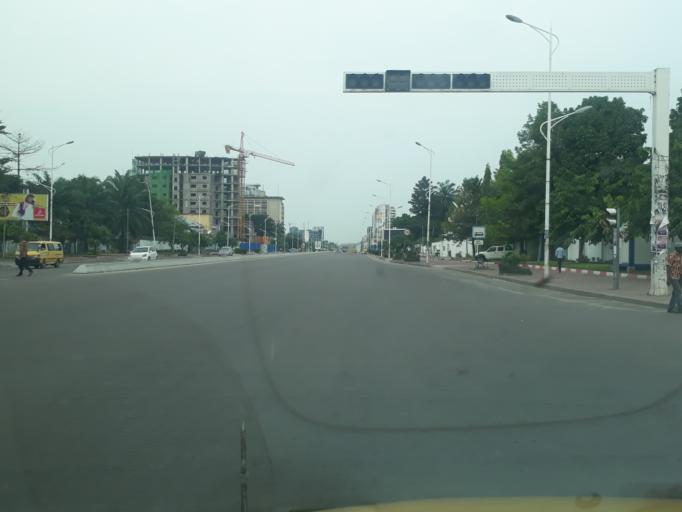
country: CD
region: Kinshasa
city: Kinshasa
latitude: -4.3170
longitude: 15.2790
